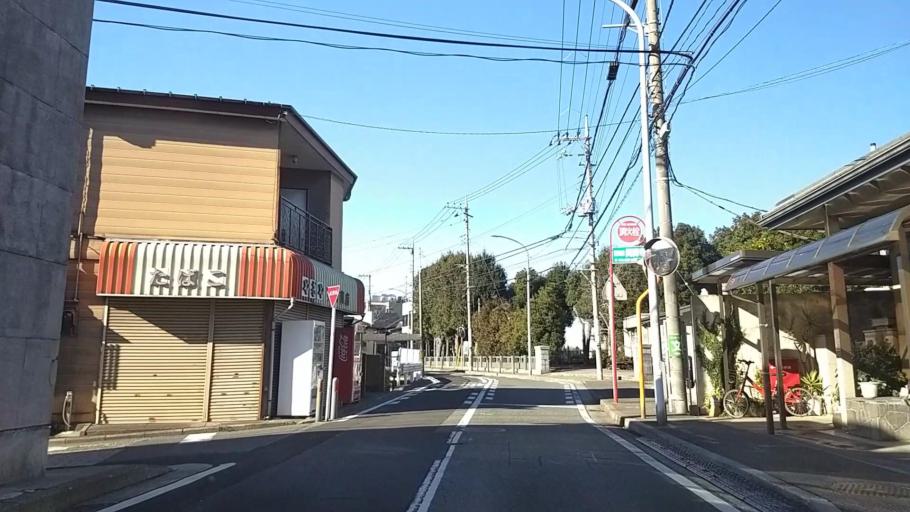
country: JP
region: Kanagawa
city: Yokohama
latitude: 35.4430
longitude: 139.6081
